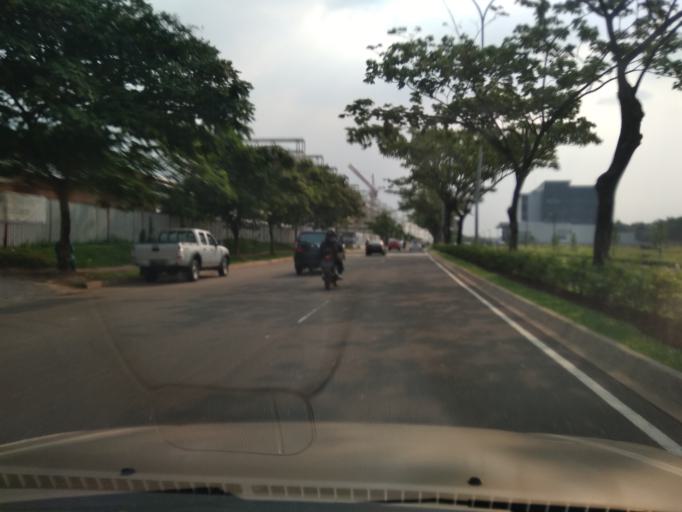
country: ID
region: West Java
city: Serpong
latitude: -6.2892
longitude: 106.6481
